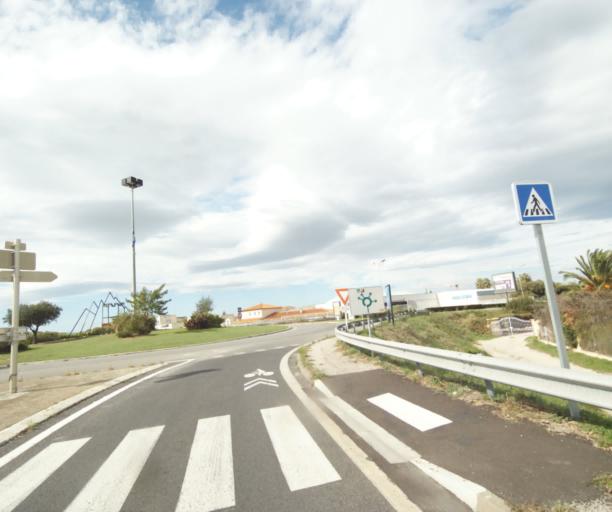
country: FR
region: Languedoc-Roussillon
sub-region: Departement des Pyrenees-Orientales
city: Argelers
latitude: 42.5513
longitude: 3.0105
